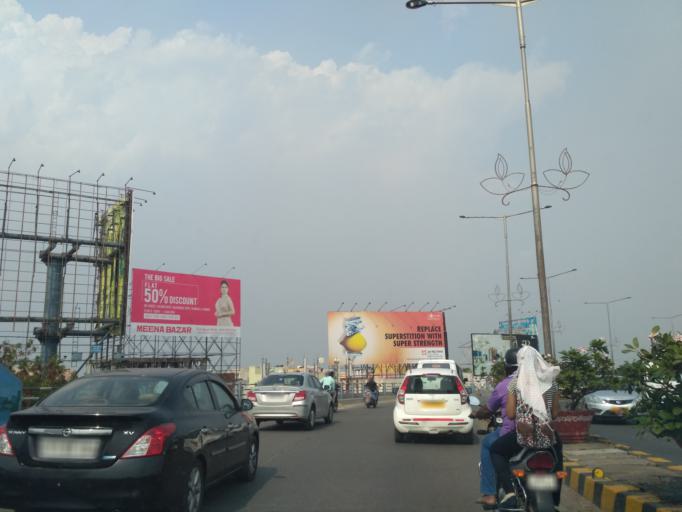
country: IN
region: Telangana
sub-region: Hyderabad
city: Hyderabad
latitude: 17.4157
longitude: 78.4612
